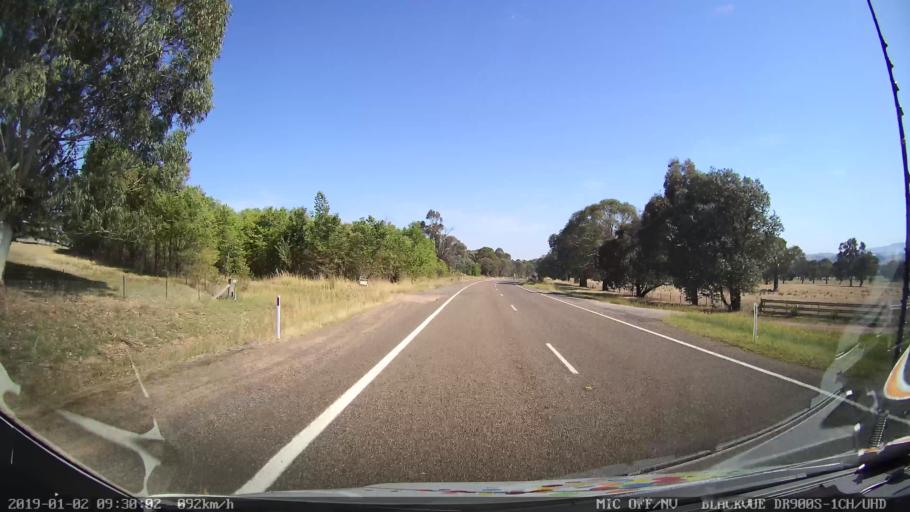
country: AU
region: New South Wales
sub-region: Tumut Shire
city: Tumut
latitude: -35.3317
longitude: 148.2381
